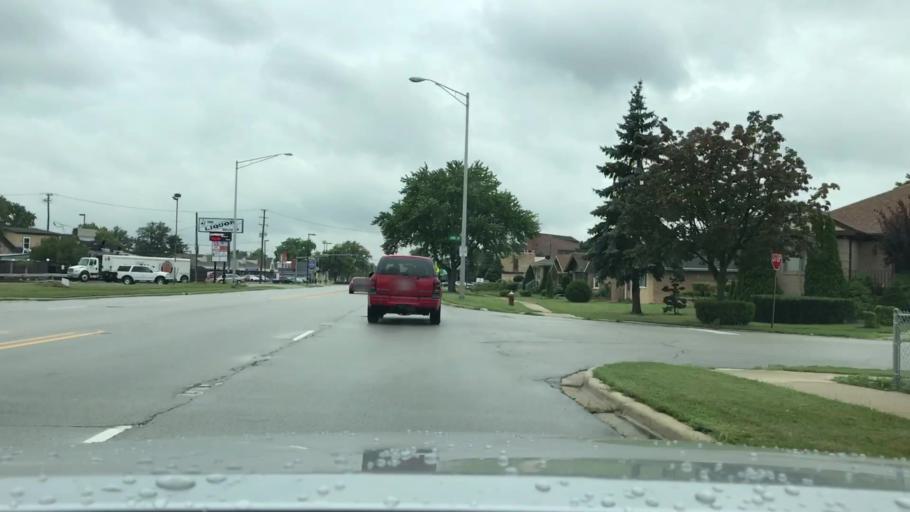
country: US
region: Illinois
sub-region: Cook County
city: Burbank
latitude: 41.7502
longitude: -87.7557
